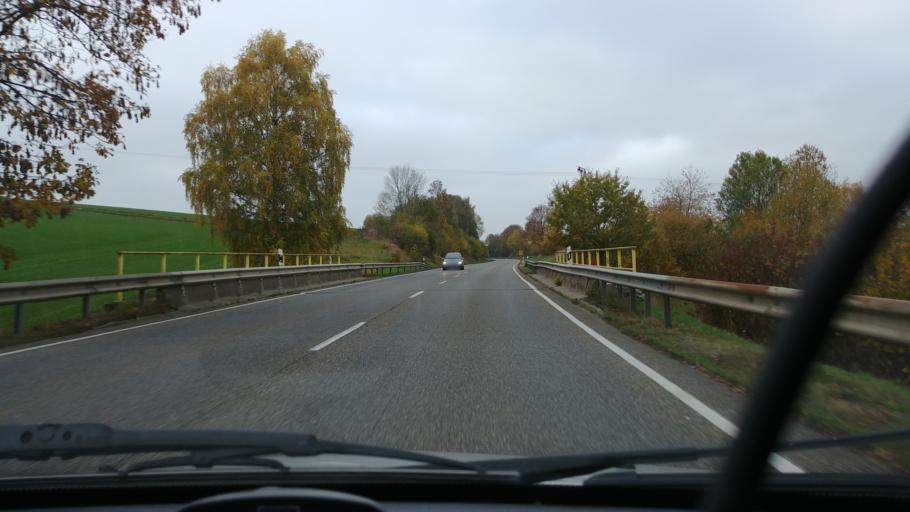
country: DE
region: Rheinland-Pfalz
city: Hachenburg
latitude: 50.6698
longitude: 7.8121
